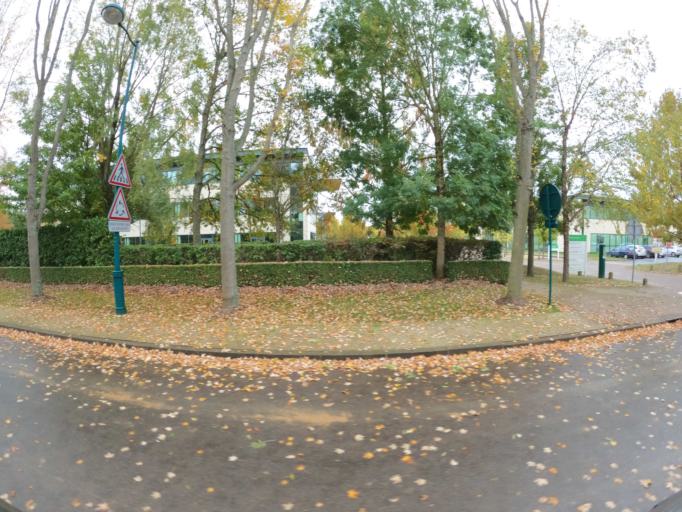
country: FR
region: Ile-de-France
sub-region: Departement de Seine-et-Marne
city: Serris
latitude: 48.8397
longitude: 2.7906
